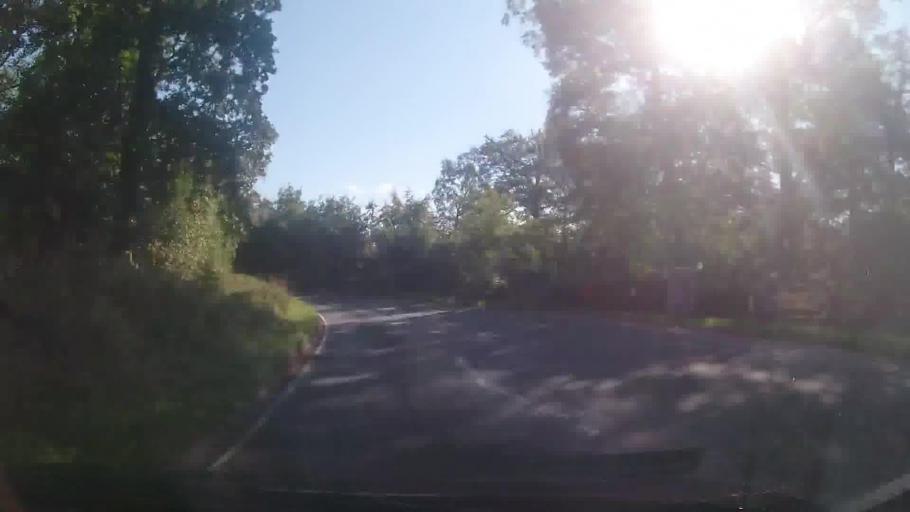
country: GB
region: England
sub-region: Cumbria
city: Seascale
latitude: 54.3579
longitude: -3.3818
